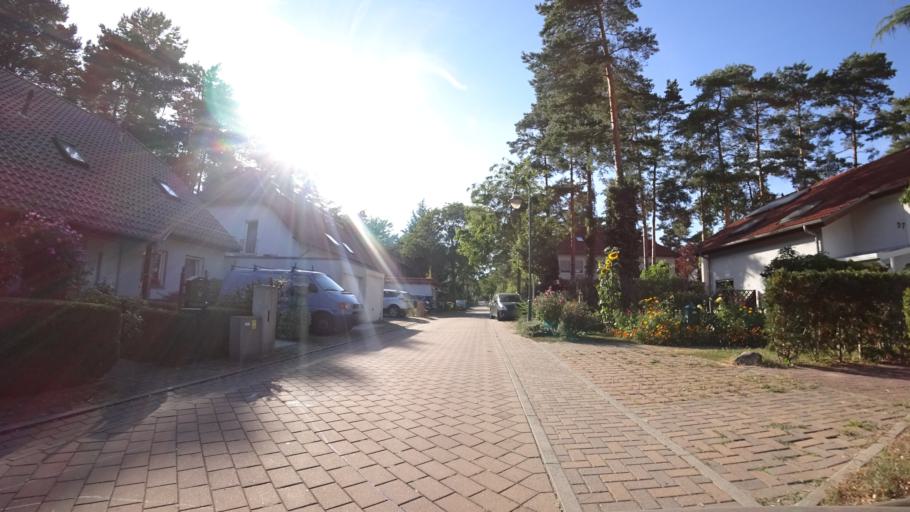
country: DE
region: Brandenburg
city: Stahnsdorf
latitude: 52.3985
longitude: 13.2029
